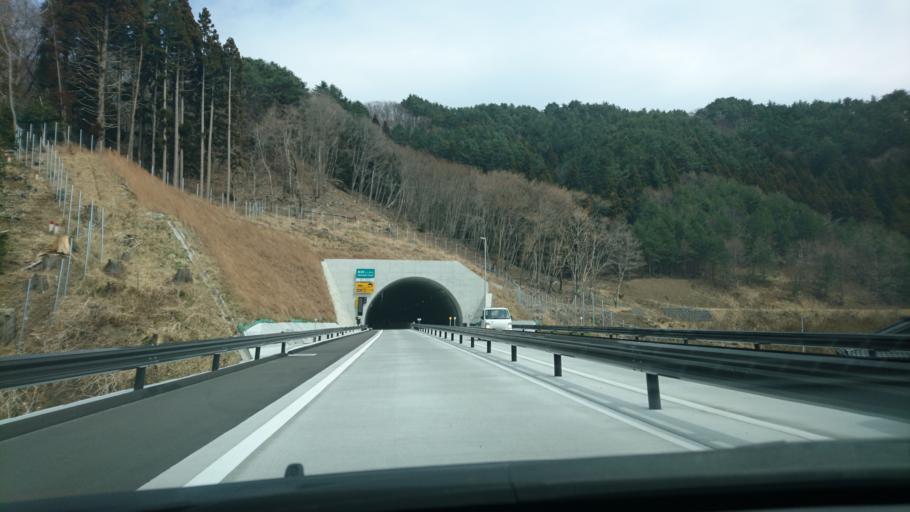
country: JP
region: Iwate
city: Kamaishi
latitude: 39.2116
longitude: 141.8646
